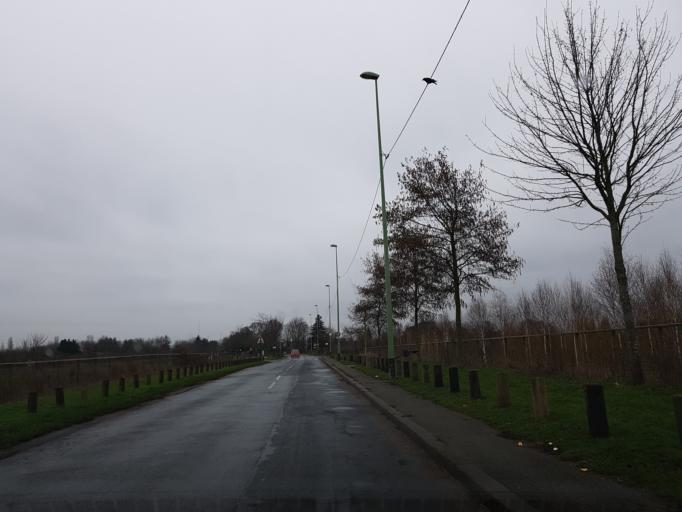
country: FR
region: Ile-de-France
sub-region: Departement du Val-de-Marne
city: Thiais
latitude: 48.7790
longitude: 2.3847
